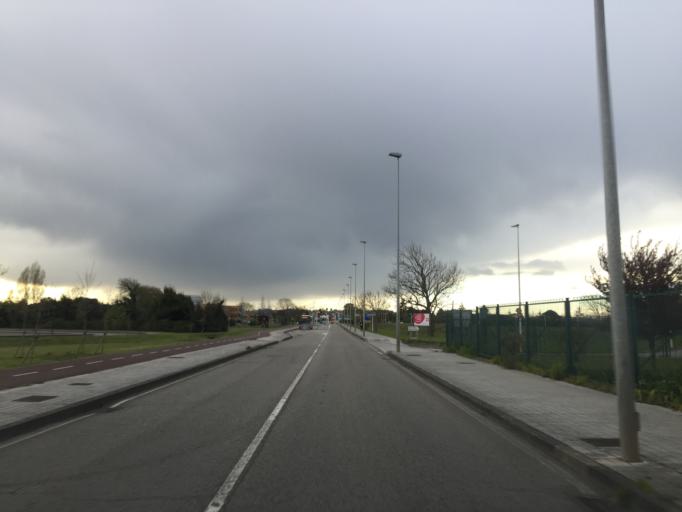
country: ES
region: Asturias
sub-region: Province of Asturias
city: Gijon
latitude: 43.5250
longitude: -5.6242
